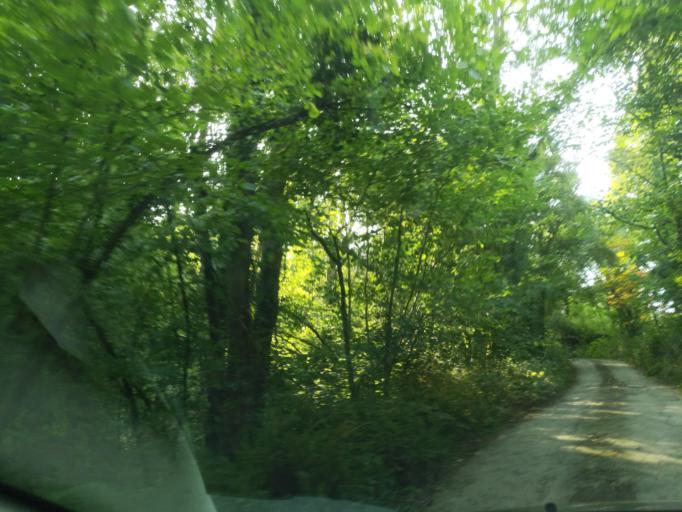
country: GB
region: England
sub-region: Devon
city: Winkleigh
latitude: 50.9665
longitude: -3.9659
